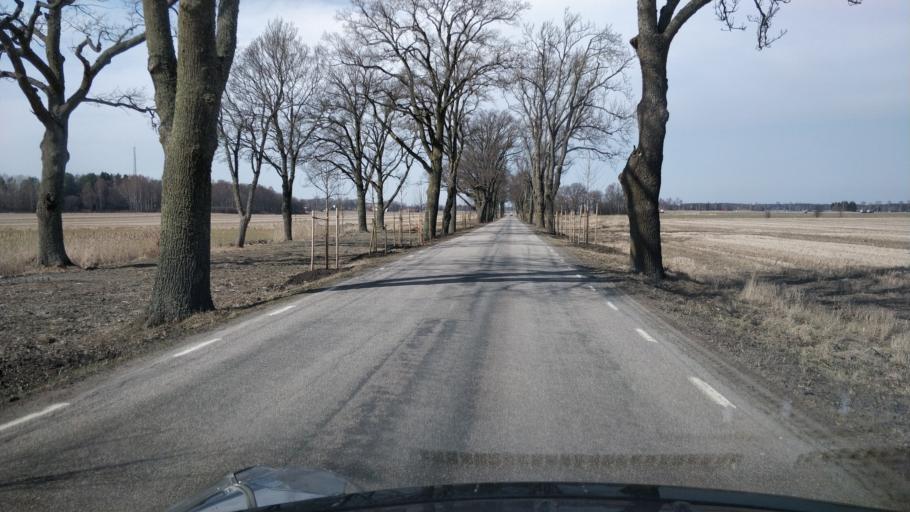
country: SE
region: Uppsala
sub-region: Enkopings Kommun
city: Enkoping
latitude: 59.6103
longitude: 17.0430
